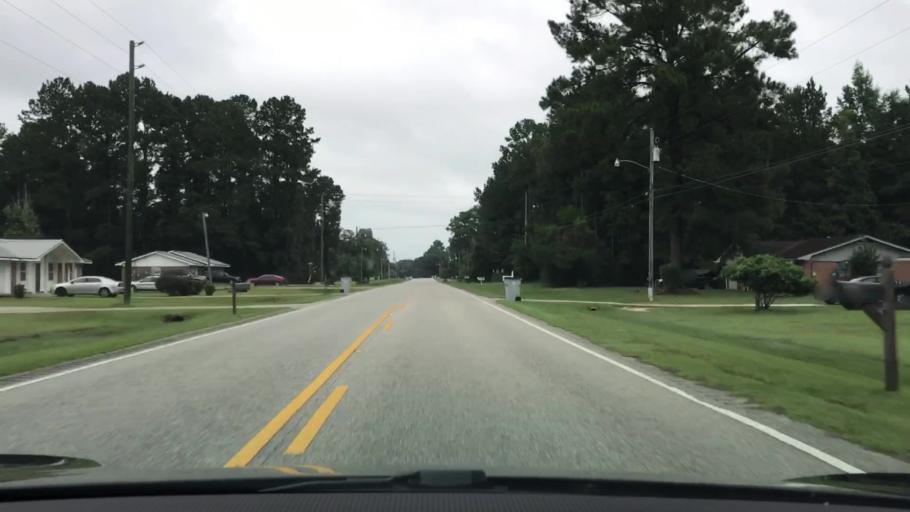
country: US
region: Alabama
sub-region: Coffee County
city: Elba
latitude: 31.3858
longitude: -86.0852
